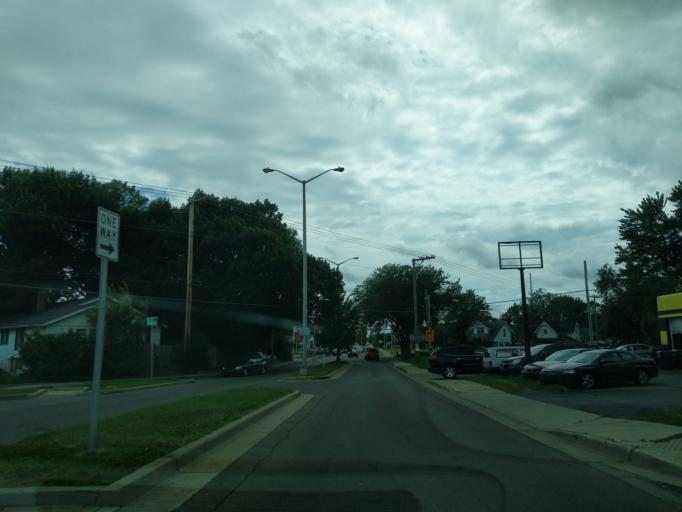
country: US
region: Indiana
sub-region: Madison County
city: Anderson
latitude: 40.0947
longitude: -85.6908
